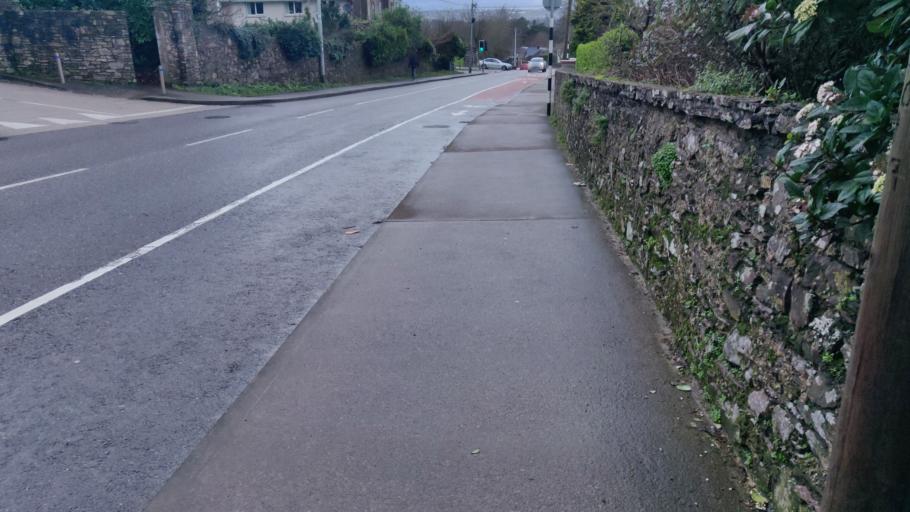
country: IE
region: Munster
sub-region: County Cork
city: Cork
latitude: 51.8738
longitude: -8.4244
